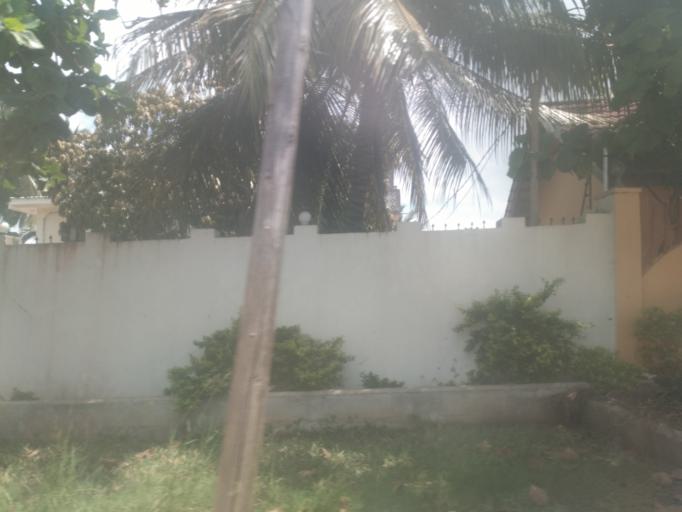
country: TZ
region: Zanzibar Urban/West
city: Zanzibar
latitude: -6.2158
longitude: 39.2120
